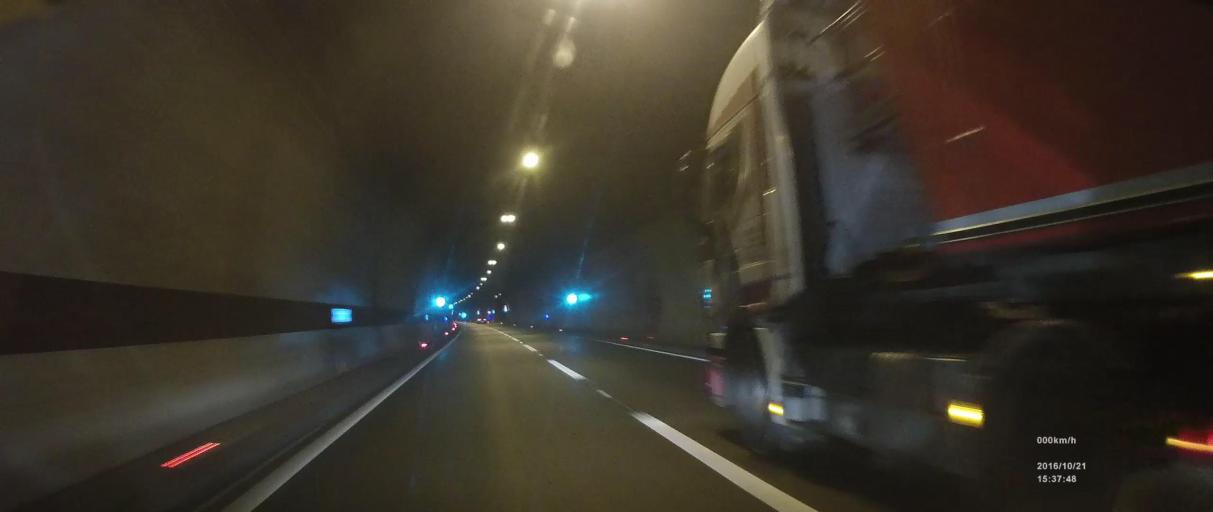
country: HR
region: Zadarska
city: Obrovac
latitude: 44.2952
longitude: 15.6731
